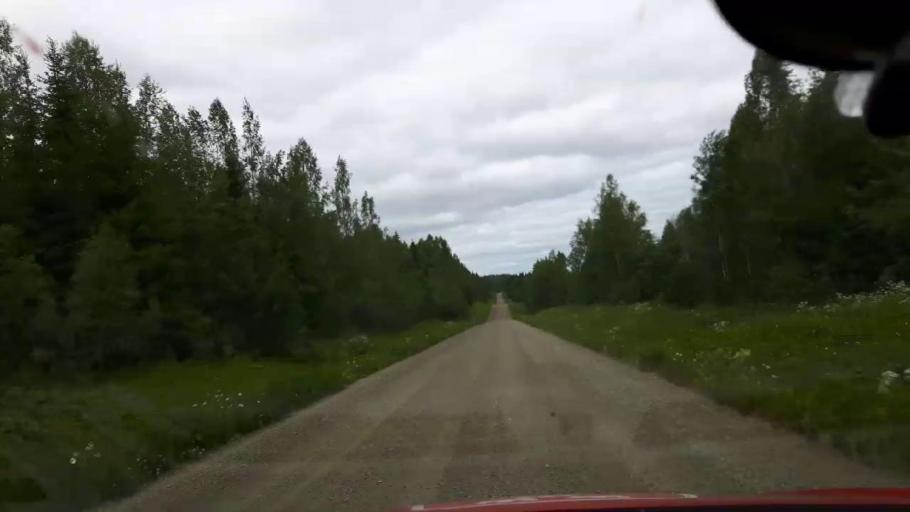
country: SE
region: Jaemtland
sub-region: OEstersunds Kommun
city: Brunflo
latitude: 62.9360
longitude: 14.9939
